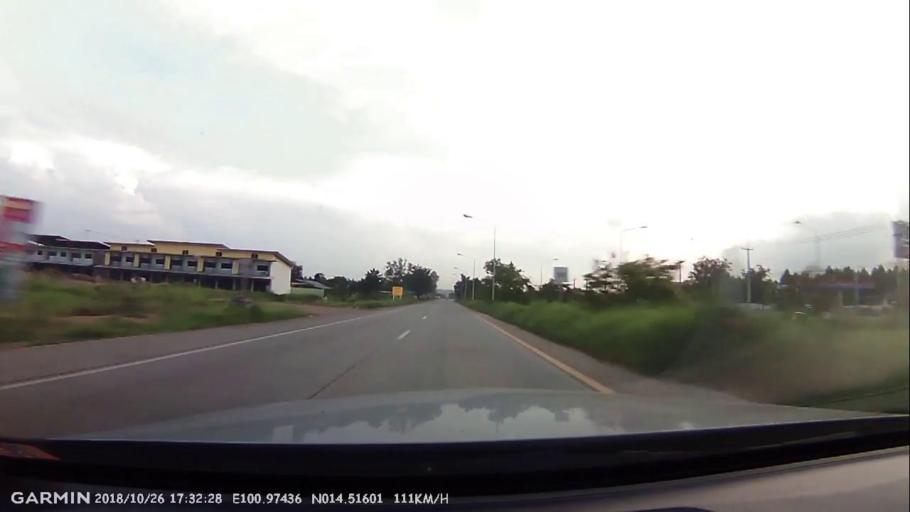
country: TH
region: Sara Buri
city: Saraburi
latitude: 14.5158
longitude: 100.9743
